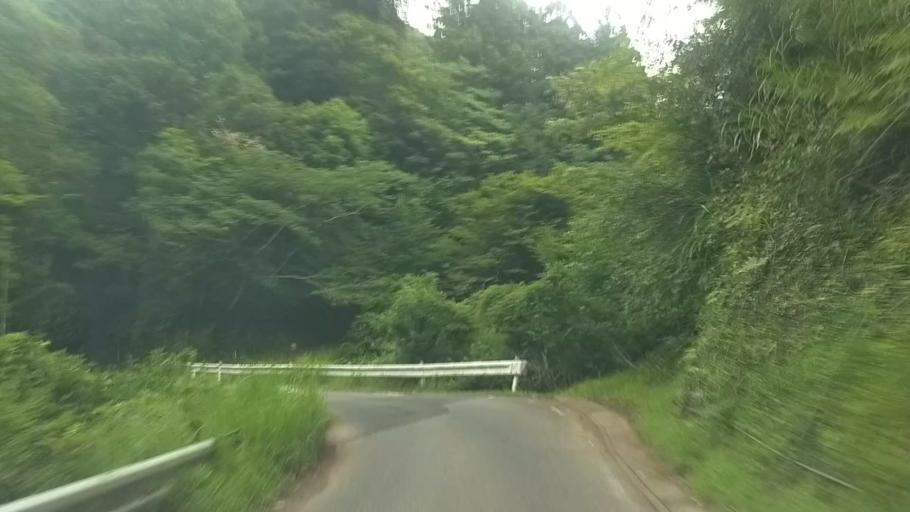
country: JP
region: Chiba
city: Kawaguchi
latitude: 35.2043
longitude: 140.1399
